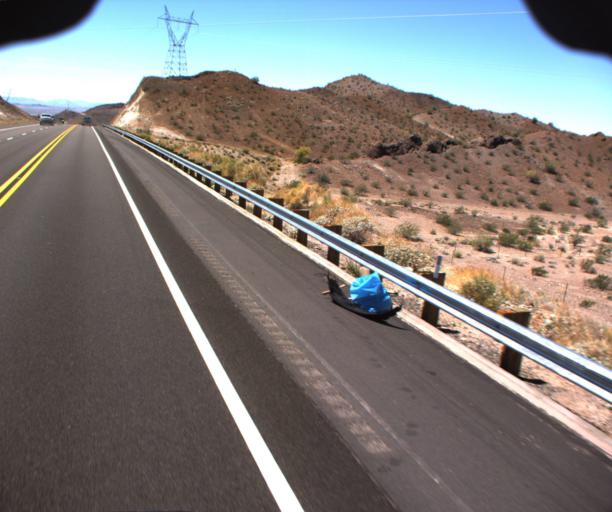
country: US
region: Arizona
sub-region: Mohave County
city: Desert Hills
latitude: 34.6150
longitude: -114.3484
